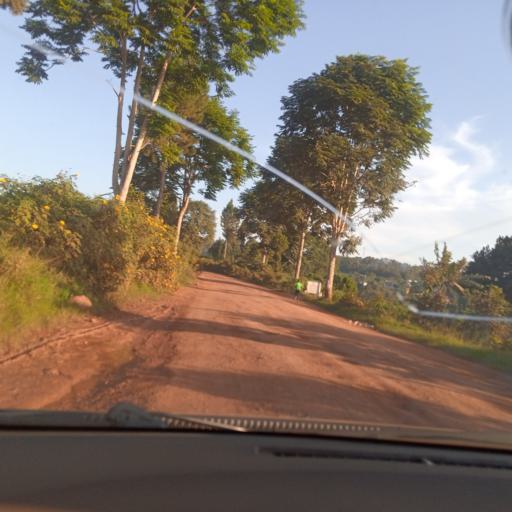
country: UG
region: Central Region
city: Masaka
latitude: -0.3318
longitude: 31.7582
